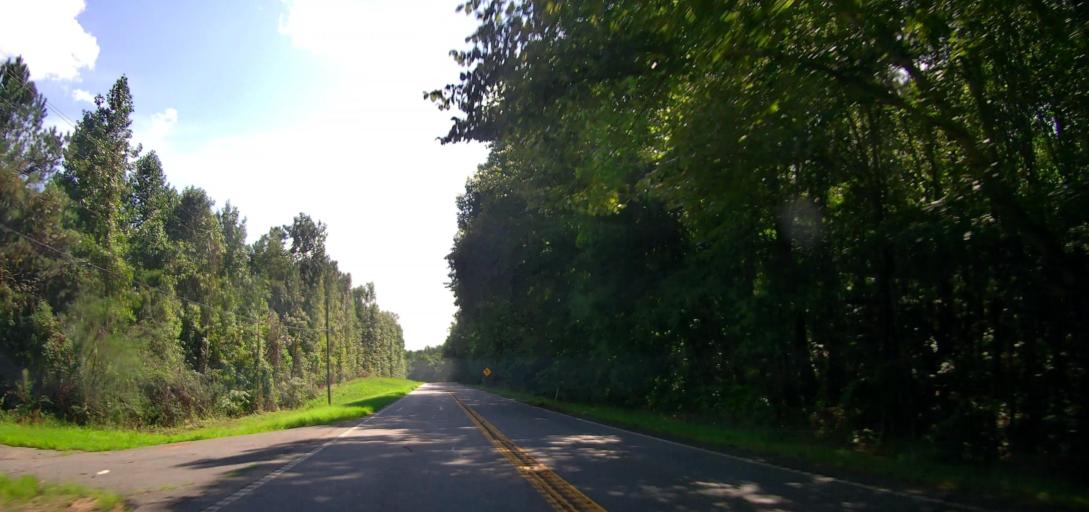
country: US
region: Georgia
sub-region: Talbot County
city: Talbotton
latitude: 32.7471
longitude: -84.5547
